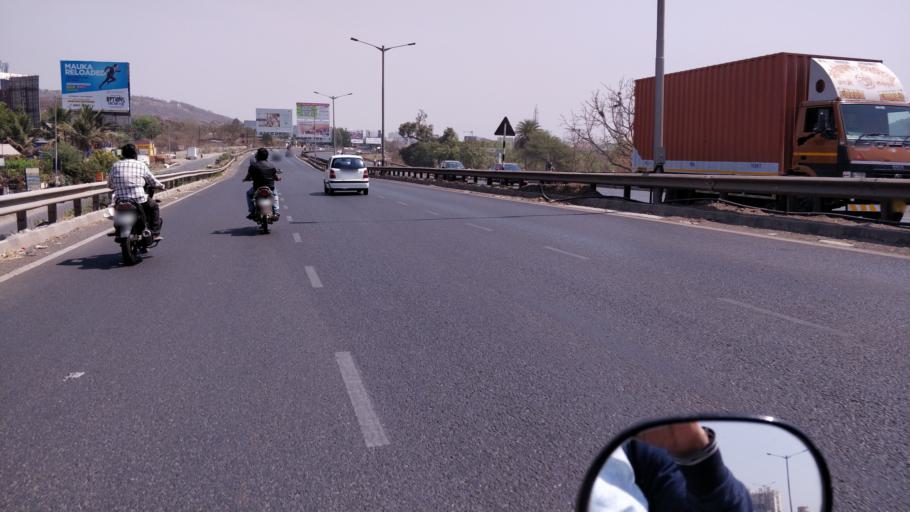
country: IN
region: Maharashtra
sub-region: Pune Division
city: Shivaji Nagar
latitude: 18.5235
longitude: 73.7708
